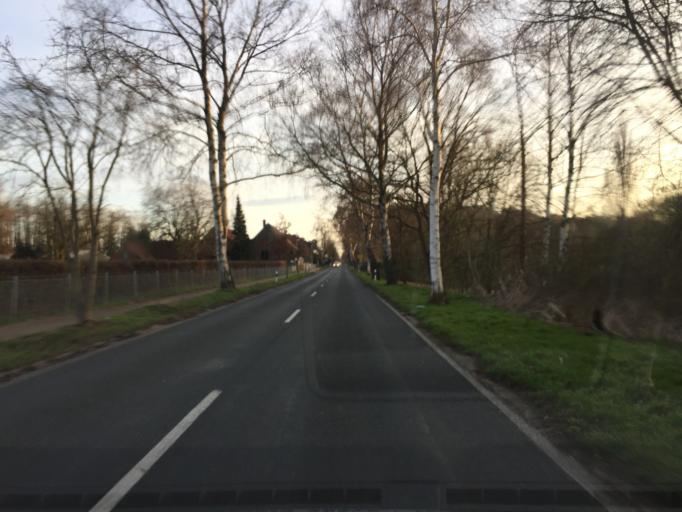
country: DE
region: Lower Saxony
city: Neustadt am Rubenberge
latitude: 52.4746
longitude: 9.4909
